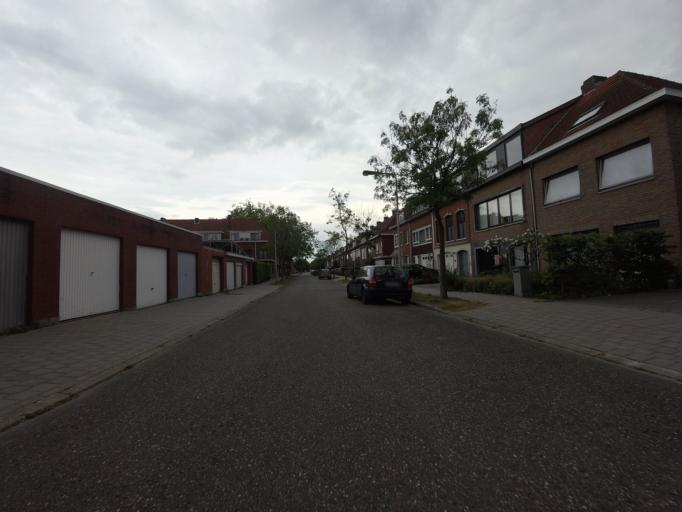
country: BE
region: Flanders
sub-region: Provincie Antwerpen
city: Edegem
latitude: 51.1648
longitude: 4.4188
